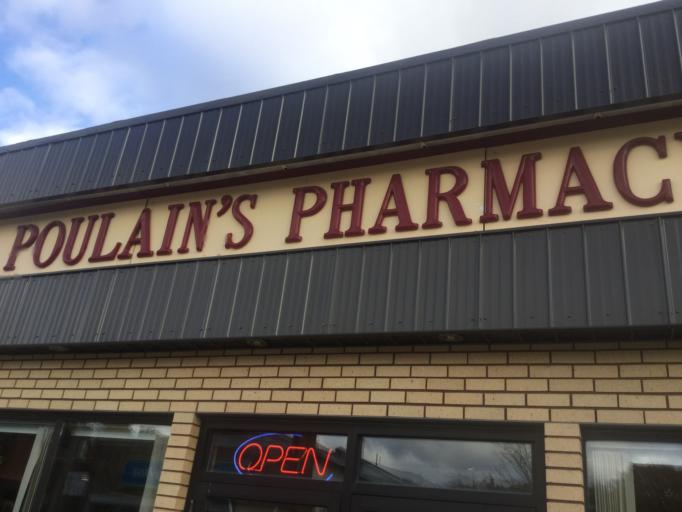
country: CA
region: Nova Scotia
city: New Glasgow
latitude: 45.5579
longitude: -62.6600
